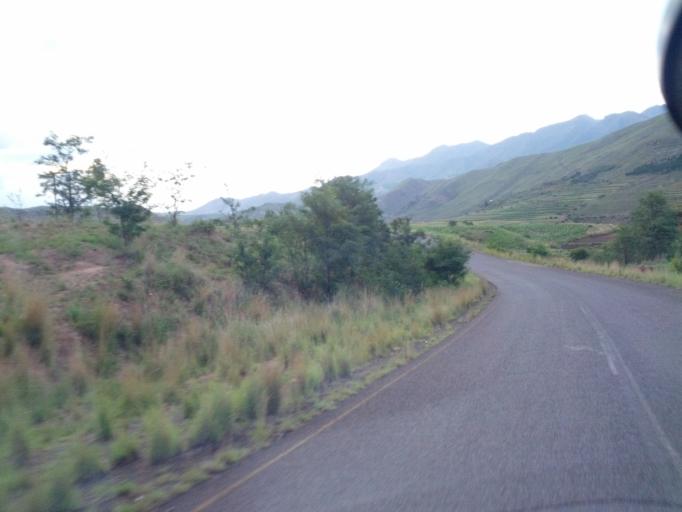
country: LS
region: Qacha's Nek
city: Qacha's Nek
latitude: -30.0678
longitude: 28.5551
